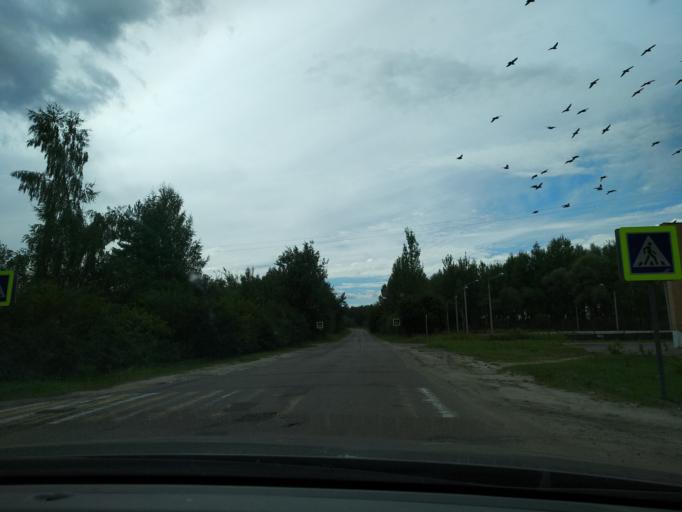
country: RU
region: Moskovskaya
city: Krasnyy Tkach
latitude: 55.3799
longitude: 39.2256
